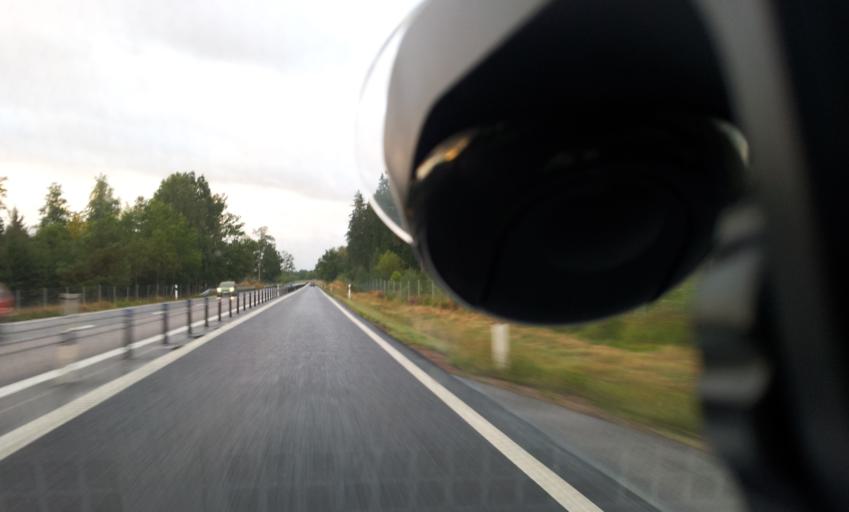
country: SE
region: Kalmar
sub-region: Monsteras Kommun
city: Timmernabben
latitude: 56.9252
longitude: 16.3854
